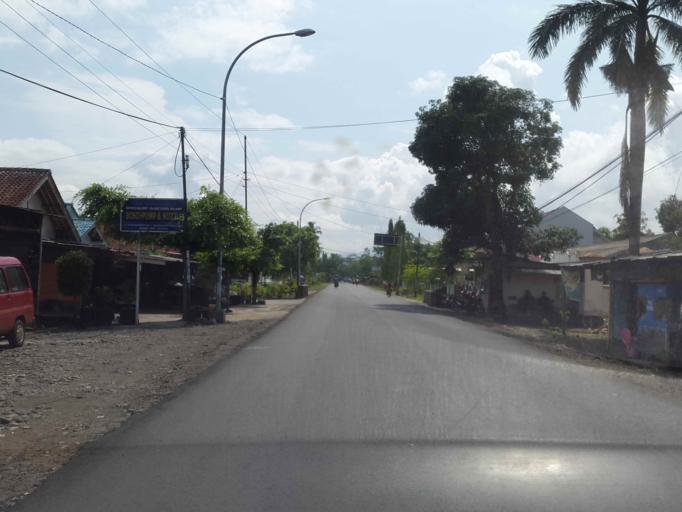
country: ID
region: Central Java
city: Banyumas
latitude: -7.5172
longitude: 109.2963
